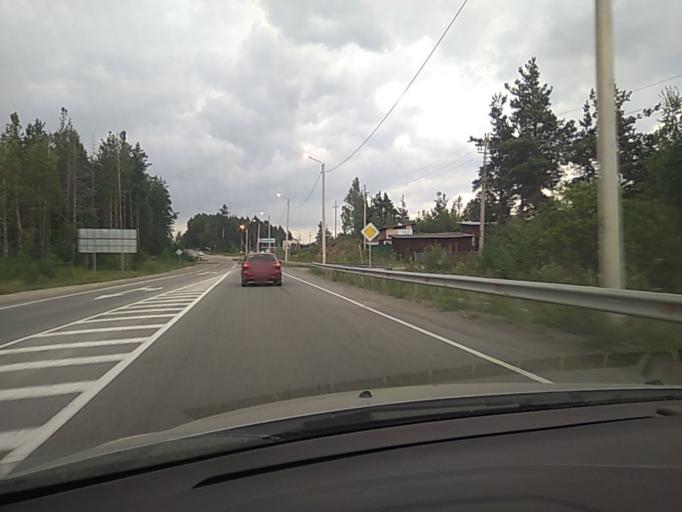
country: RU
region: Chelyabinsk
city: Kyshtym
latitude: 55.7146
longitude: 60.5102
